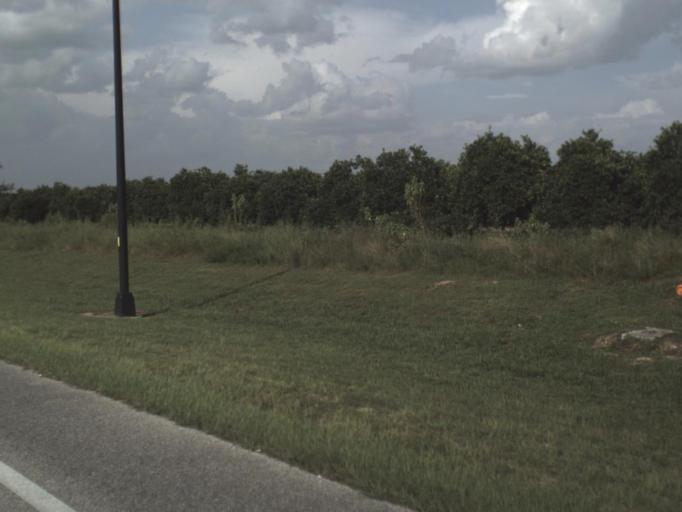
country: US
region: Florida
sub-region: Polk County
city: Davenport
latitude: 28.1724
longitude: -81.6397
